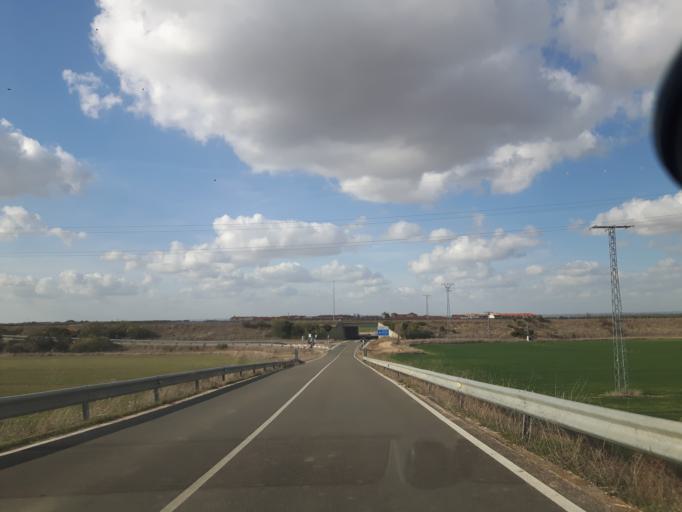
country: ES
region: Castille and Leon
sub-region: Provincia de Salamanca
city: Moriscos
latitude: 41.0119
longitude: -5.5852
